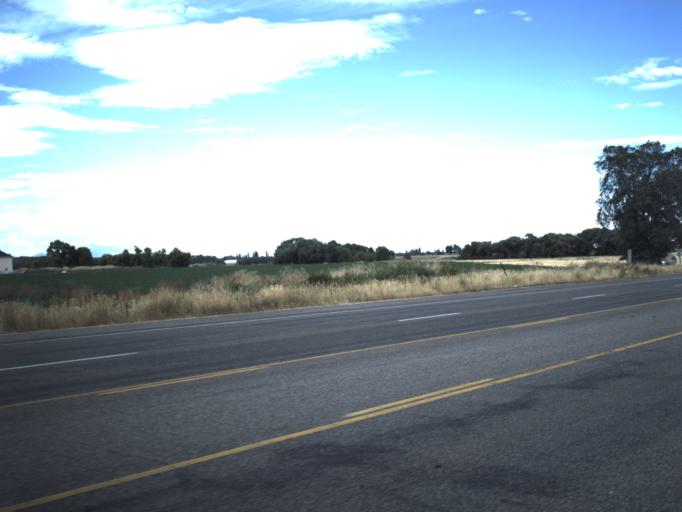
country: US
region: Utah
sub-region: Cache County
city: Wellsville
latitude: 41.6501
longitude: -111.9087
